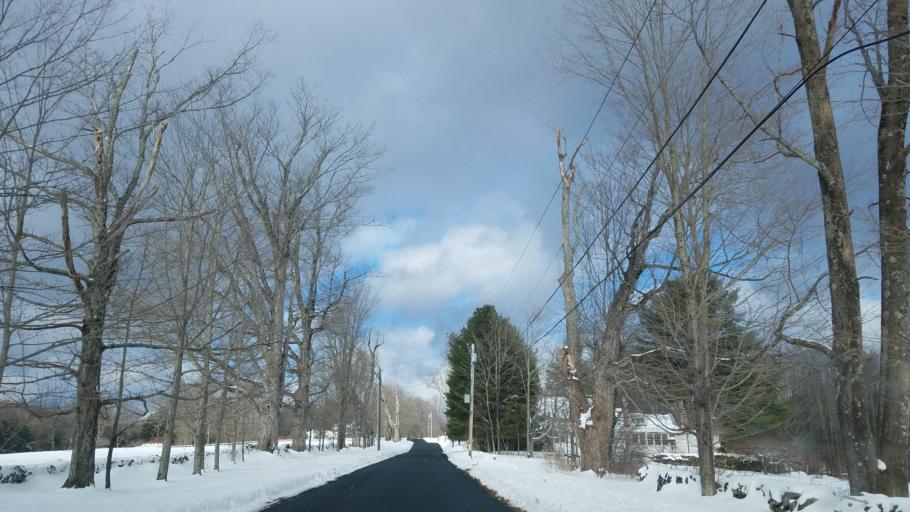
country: US
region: Connecticut
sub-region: Litchfield County
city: Winsted
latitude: 41.9780
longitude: -73.0815
